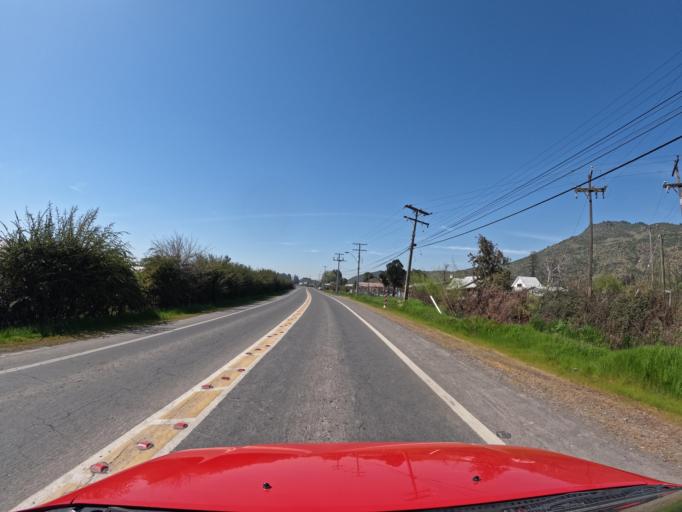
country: CL
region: Maule
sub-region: Provincia de Curico
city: Rauco
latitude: -35.0075
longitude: -71.4052
